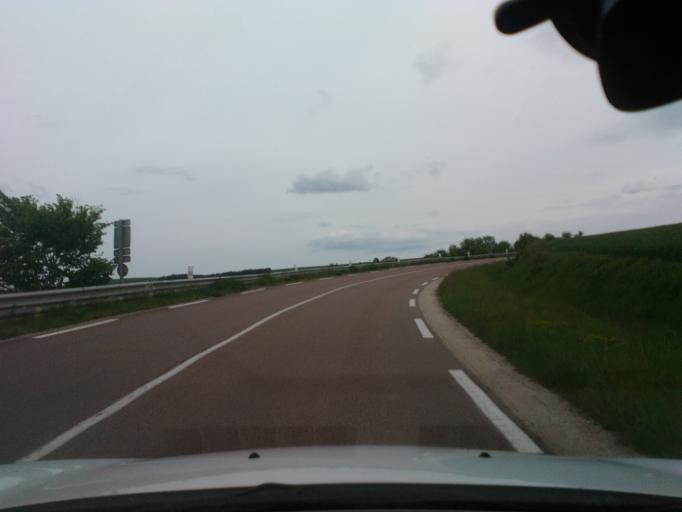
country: FR
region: Champagne-Ardenne
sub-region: Departement de l'Aube
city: Bar-sur-Aube
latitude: 48.2226
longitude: 4.8134
